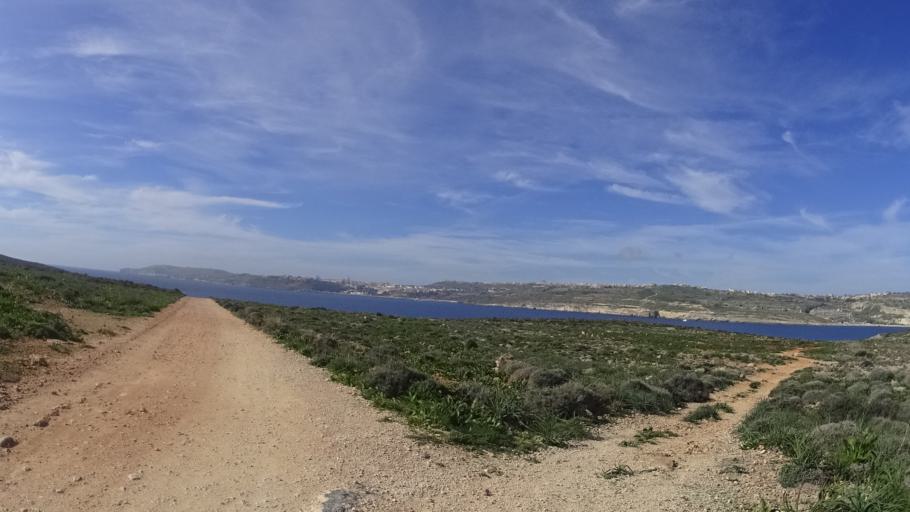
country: MT
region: Il-Qala
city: Qala
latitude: 36.0151
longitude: 14.3267
